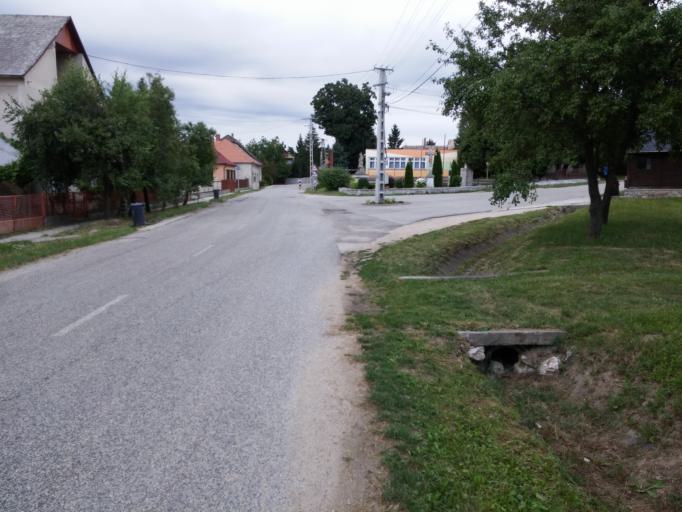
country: HU
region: Veszprem
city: Cseteny
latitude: 47.2581
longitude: 18.0303
